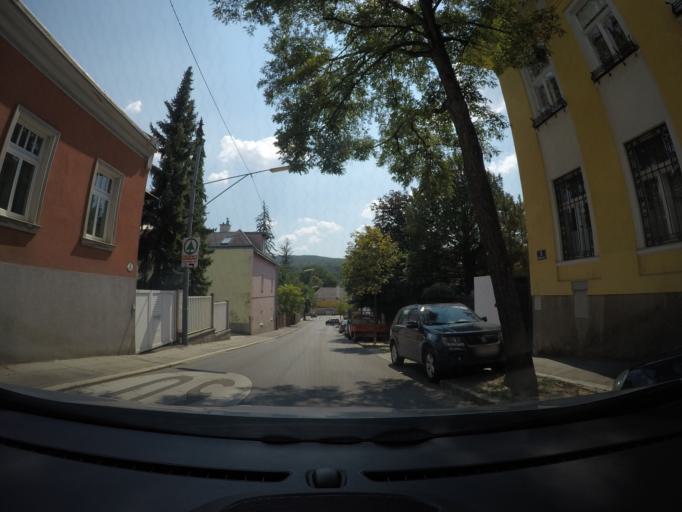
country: AT
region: Lower Austria
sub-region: Politischer Bezirk Wien-Umgebung
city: Purkersdorf
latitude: 48.2048
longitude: 16.2522
